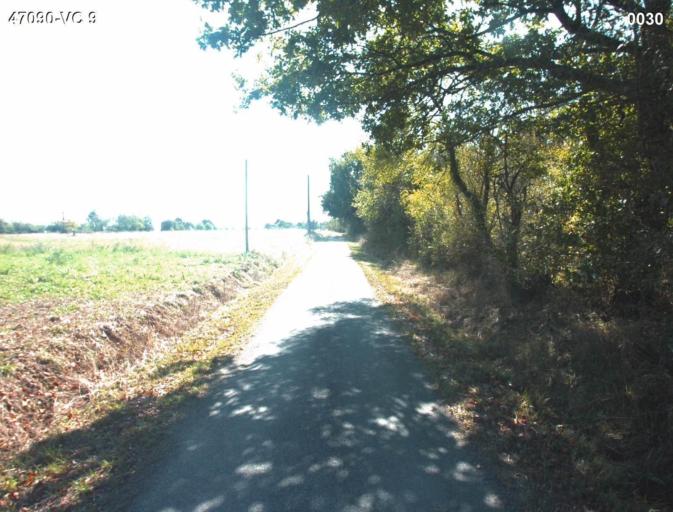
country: FR
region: Aquitaine
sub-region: Departement du Lot-et-Garonne
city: Nerac
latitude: 44.1856
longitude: 0.3870
